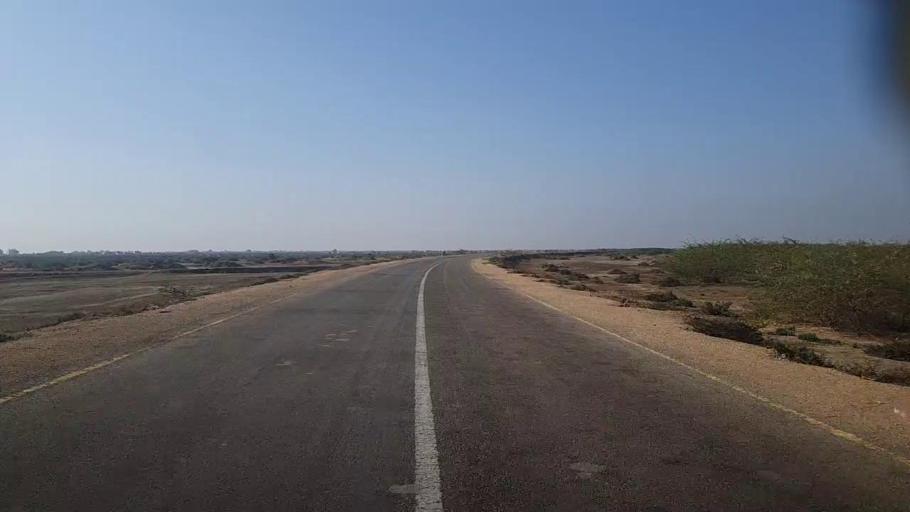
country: PK
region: Sindh
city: Mirpur Sakro
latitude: 24.5601
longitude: 67.4986
